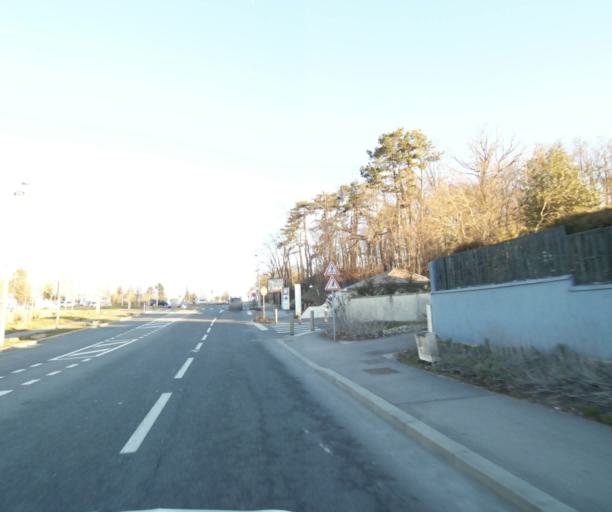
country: FR
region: Lorraine
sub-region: Departement de Meurthe-et-Moselle
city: Laxou
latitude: 48.7002
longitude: 6.1368
